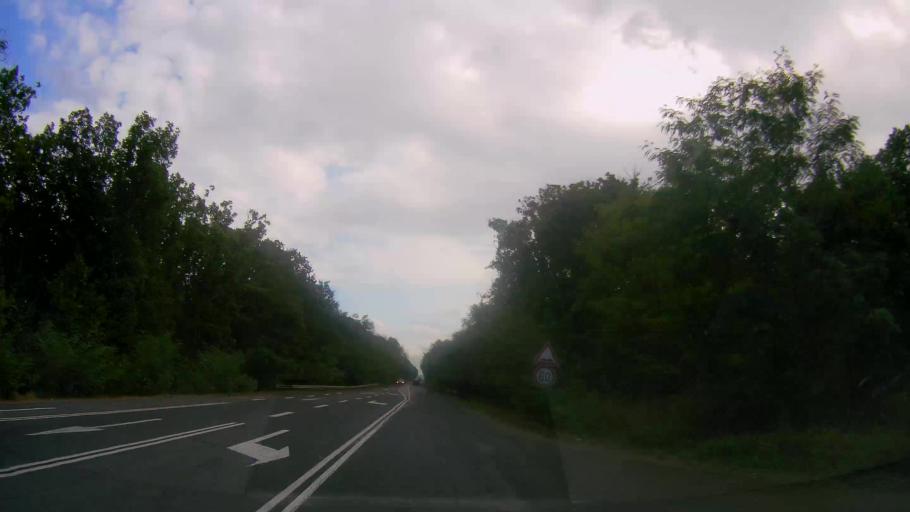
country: BG
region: Burgas
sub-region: Obshtina Primorsko
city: Primorsko
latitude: 42.2758
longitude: 27.7403
